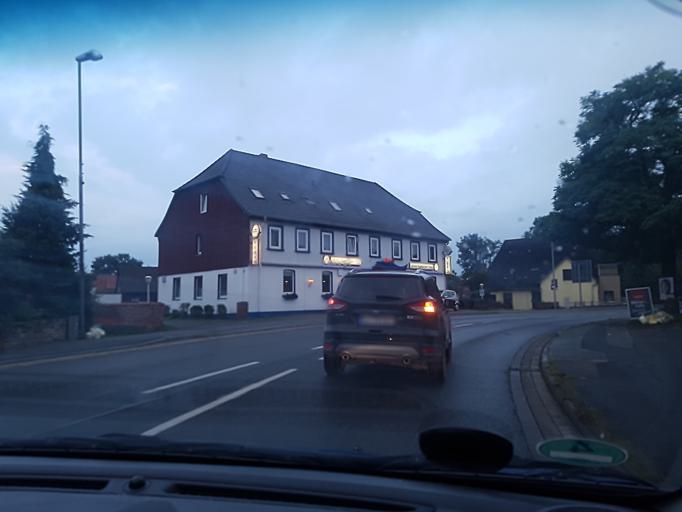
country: DE
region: Lower Saxony
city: Hemmingen
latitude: 52.3018
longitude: 9.7405
